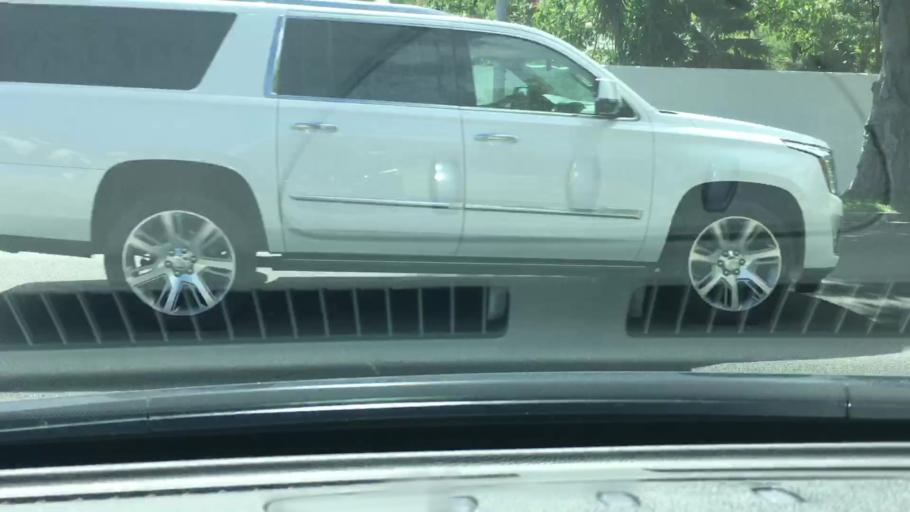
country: US
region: Hawaii
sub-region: Honolulu County
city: Waimanalo Beach
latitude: 21.2940
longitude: -157.7106
